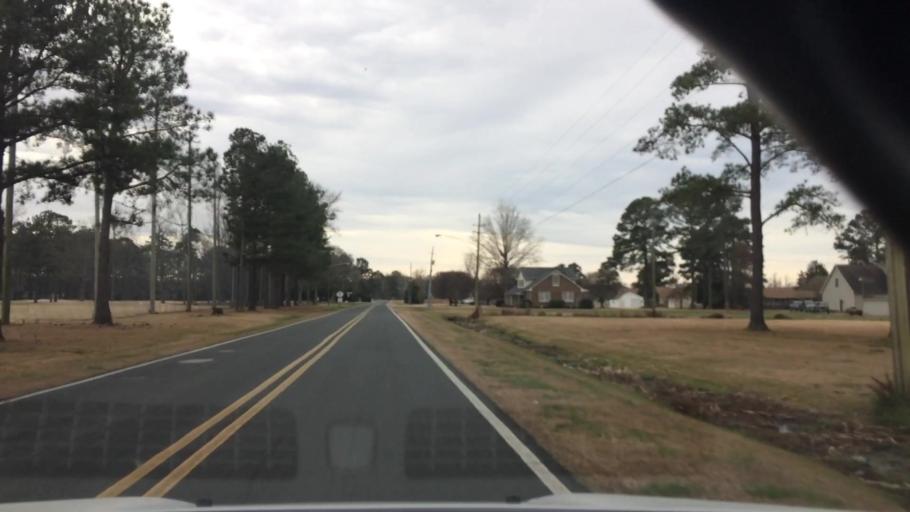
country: US
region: North Carolina
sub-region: Pitt County
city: Ayden
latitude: 35.4622
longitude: -77.3905
